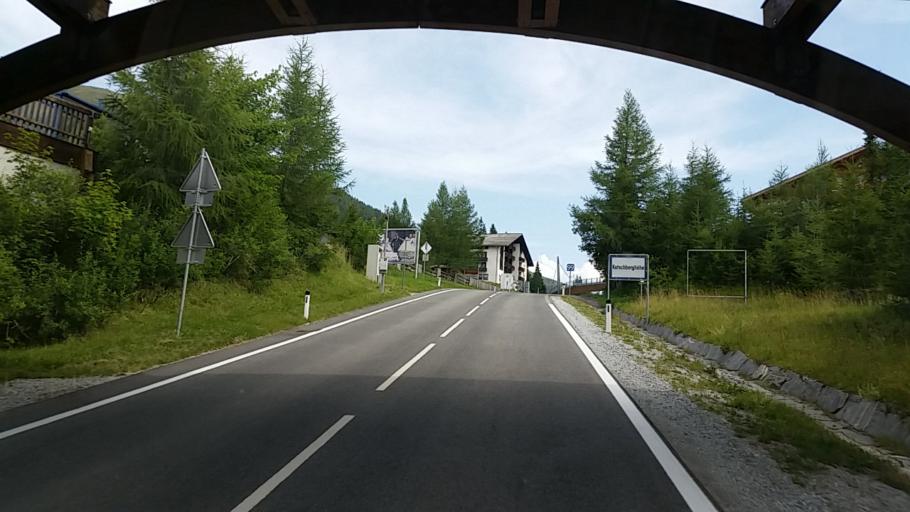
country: AT
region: Salzburg
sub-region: Politischer Bezirk Tamsweg
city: Sankt Michael im Lungau
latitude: 47.0608
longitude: 13.6139
